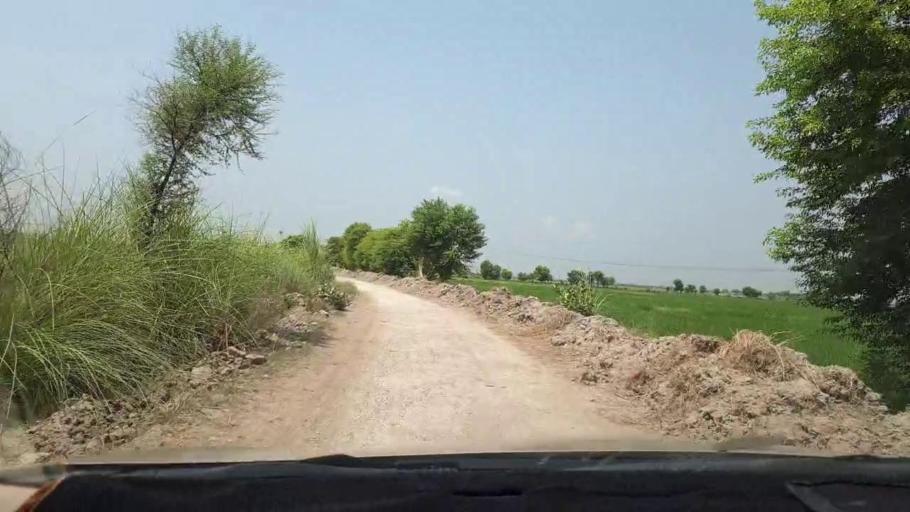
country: PK
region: Sindh
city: Naudero
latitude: 27.6649
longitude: 68.3097
